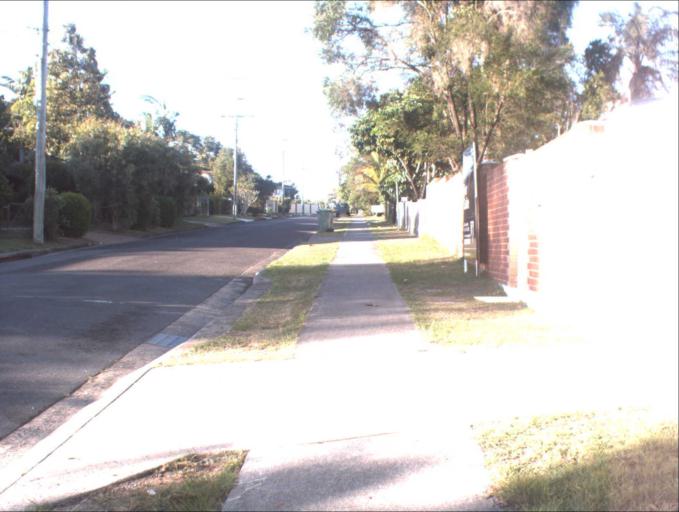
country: AU
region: Queensland
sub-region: Logan
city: Logan City
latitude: -27.6502
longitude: 153.1081
